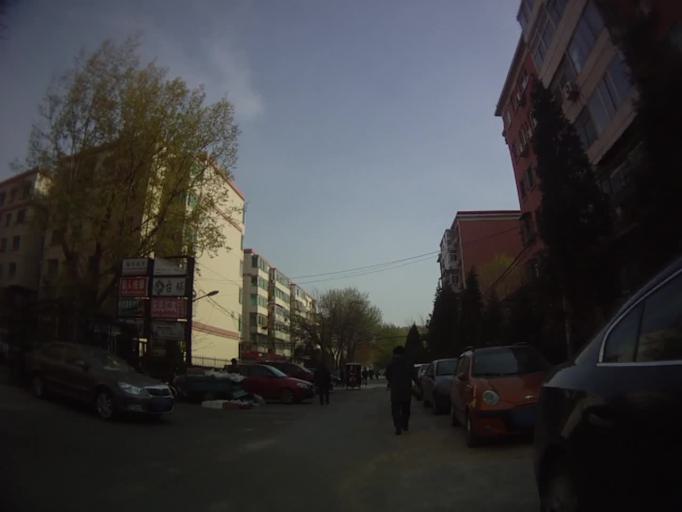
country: CN
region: Beijing
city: Chaowai
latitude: 39.8990
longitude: 116.4417
